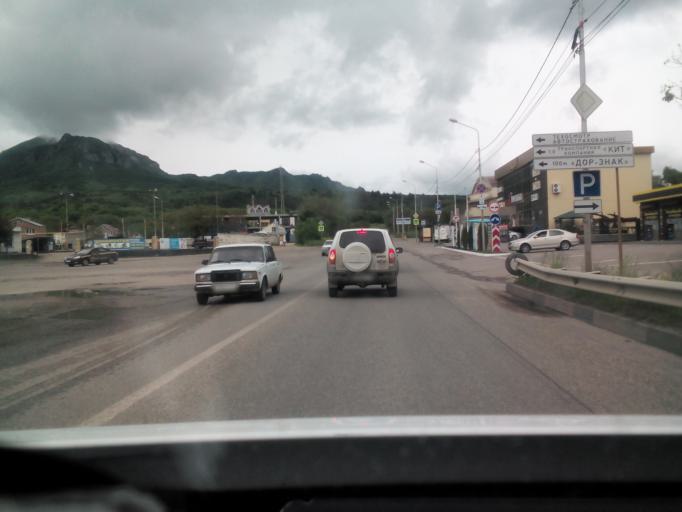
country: RU
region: Stavropol'skiy
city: Vinsady
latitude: 44.0578
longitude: 43.0088
